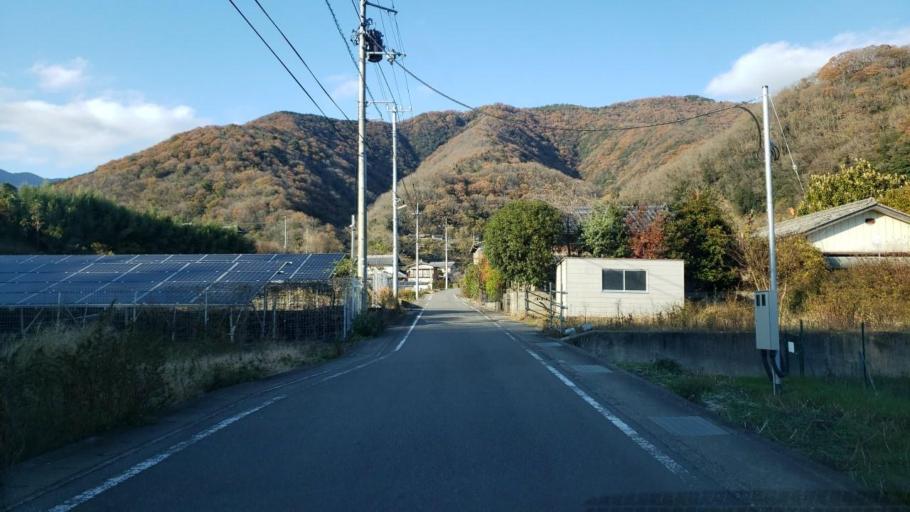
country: JP
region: Tokushima
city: Wakimachi
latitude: 34.0729
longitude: 134.0840
